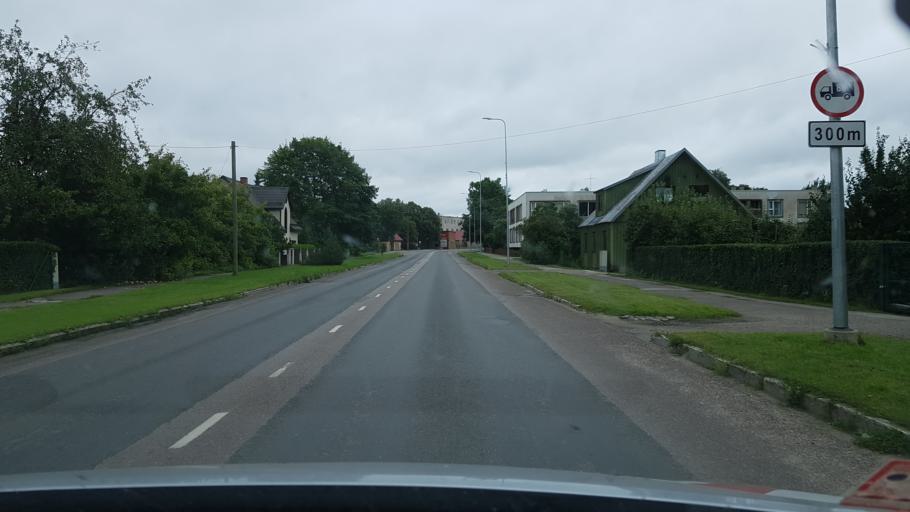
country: EE
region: Viljandimaa
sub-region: Viljandi linn
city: Viljandi
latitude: 58.3757
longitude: 25.5980
